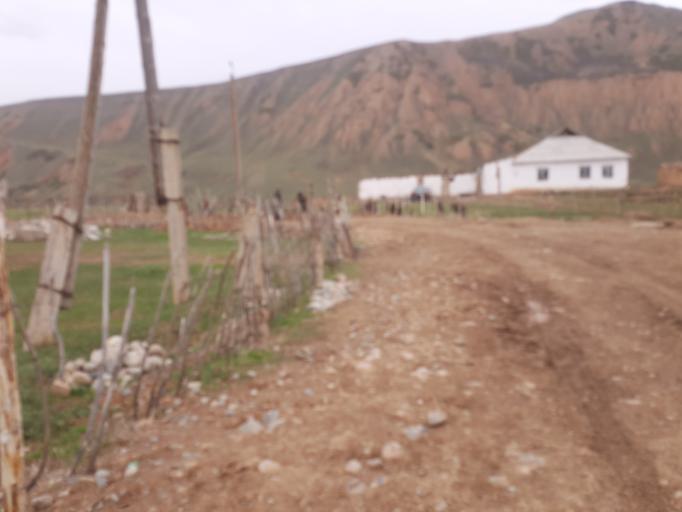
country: KG
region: Naryn
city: Naryn
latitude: 41.5195
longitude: 76.4362
